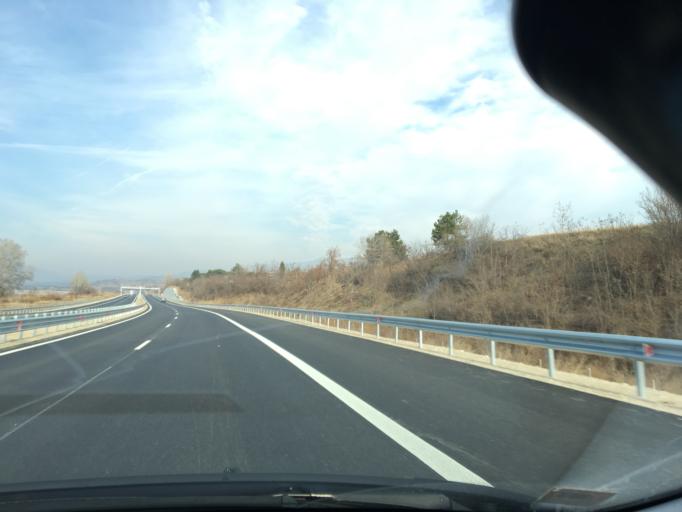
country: BG
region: Blagoevgrad
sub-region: Obshtina Sandanski
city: Sandanski
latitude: 41.5682
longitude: 23.2408
